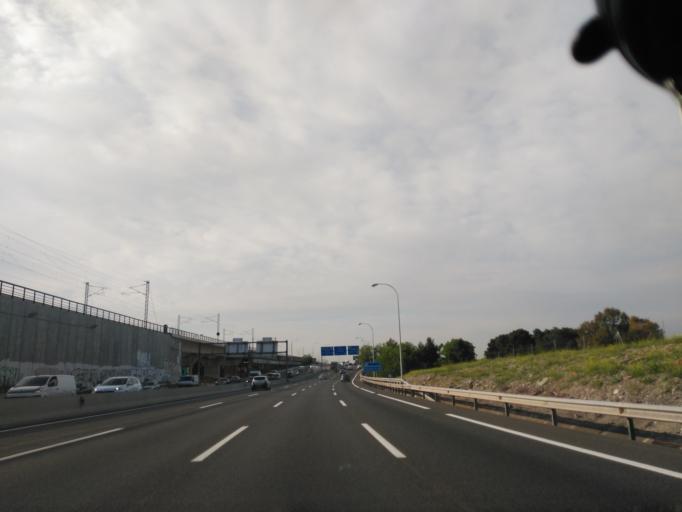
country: ES
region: Madrid
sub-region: Provincia de Madrid
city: Usera
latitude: 40.3704
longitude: -3.6791
